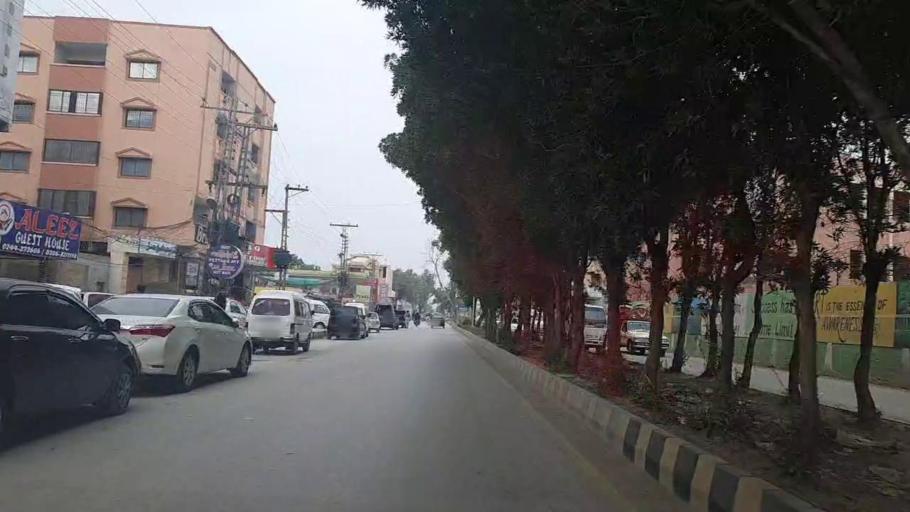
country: PK
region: Sindh
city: Nawabshah
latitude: 26.2430
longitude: 68.4016
